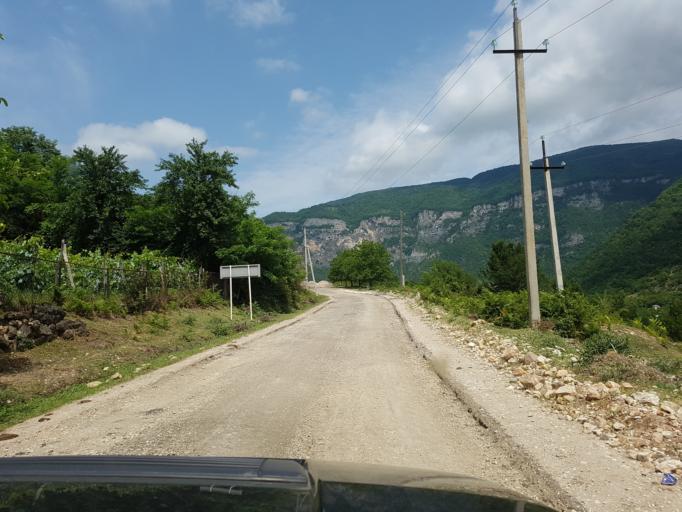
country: GE
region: Imereti
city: Tsqaltubo
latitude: 42.5001
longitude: 42.7862
